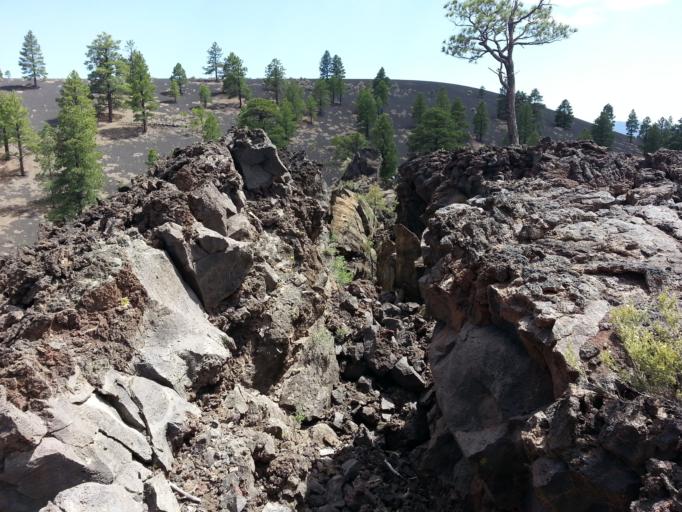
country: US
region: Arizona
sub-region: Coconino County
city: Flagstaff
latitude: 35.3628
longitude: -111.5161
